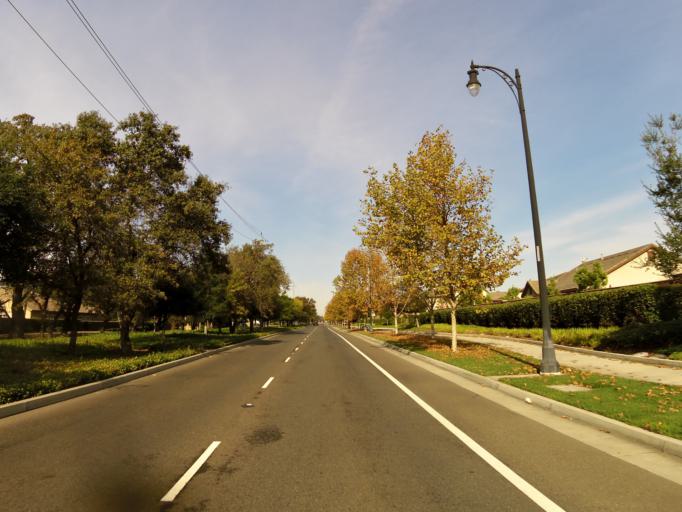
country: US
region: California
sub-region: Sacramento County
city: Laguna
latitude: 38.3993
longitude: -121.4176
